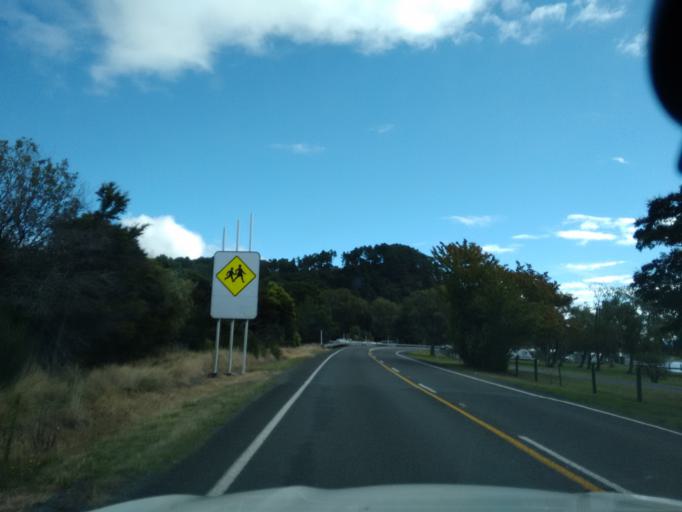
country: NZ
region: Waikato
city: Turangi
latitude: -38.8869
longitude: 175.9609
